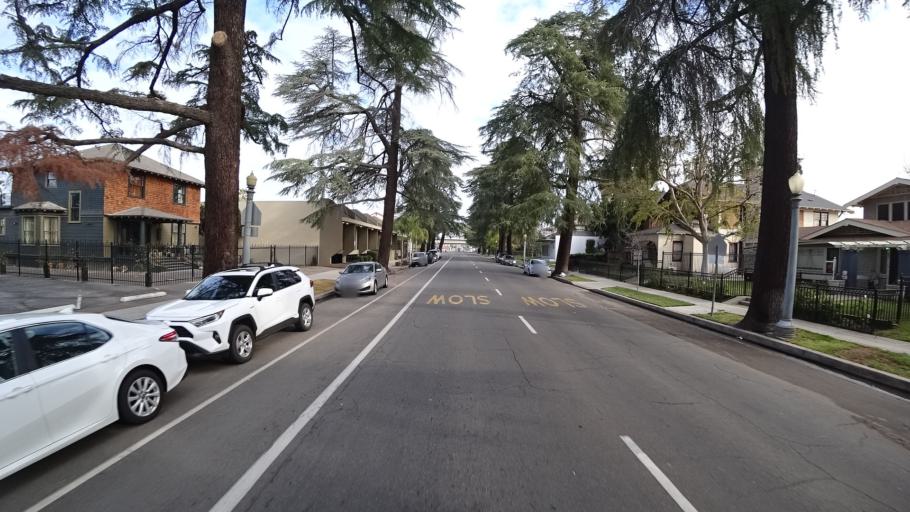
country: US
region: California
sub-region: Fresno County
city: Fresno
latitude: 36.7466
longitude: -119.8004
